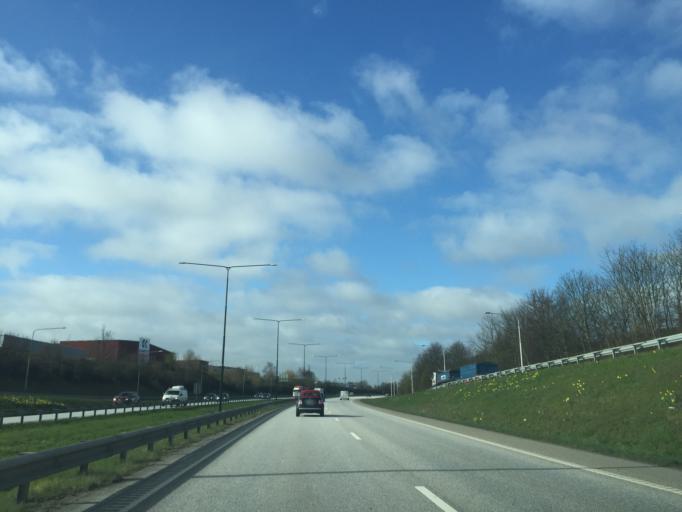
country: SE
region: Skane
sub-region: Malmo
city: Malmoe
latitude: 55.5691
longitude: 13.0442
